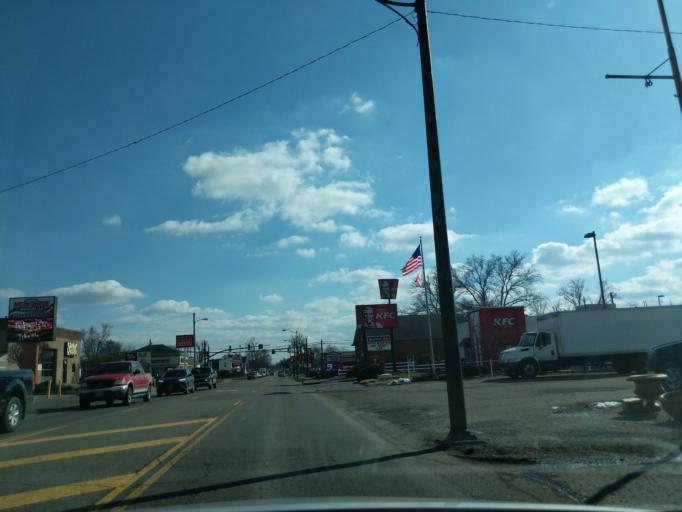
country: US
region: Ohio
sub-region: Coshocton County
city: Coshocton
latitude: 40.2734
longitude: -81.8689
